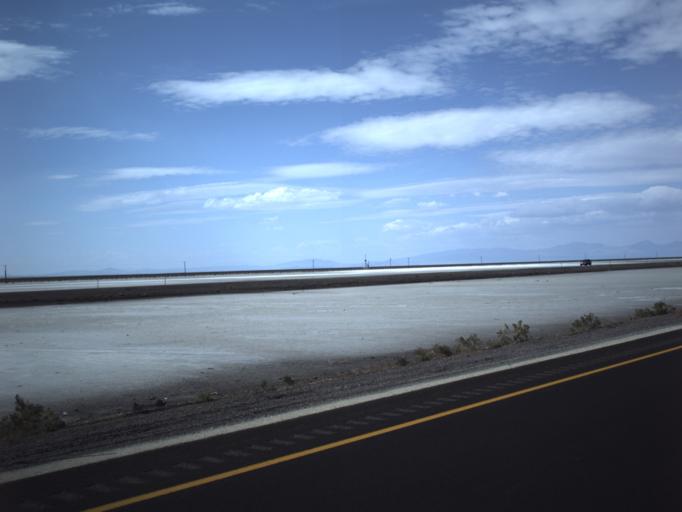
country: US
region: Utah
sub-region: Tooele County
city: Wendover
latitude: 40.7325
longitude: -113.5283
